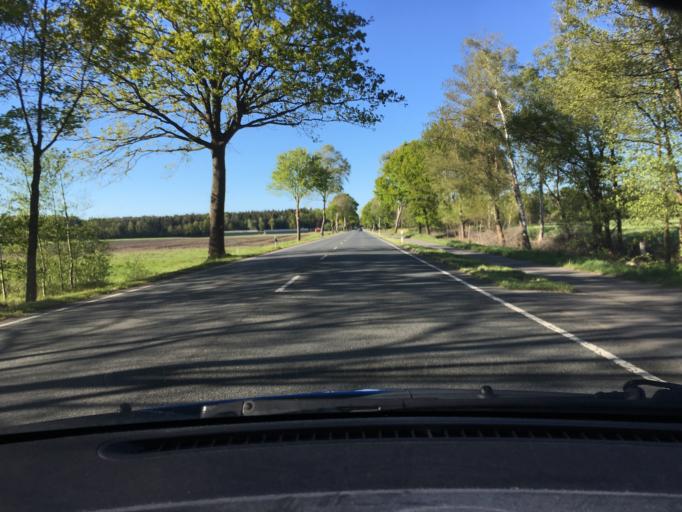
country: DE
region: Lower Saxony
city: Soltau
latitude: 53.0332
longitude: 9.8527
